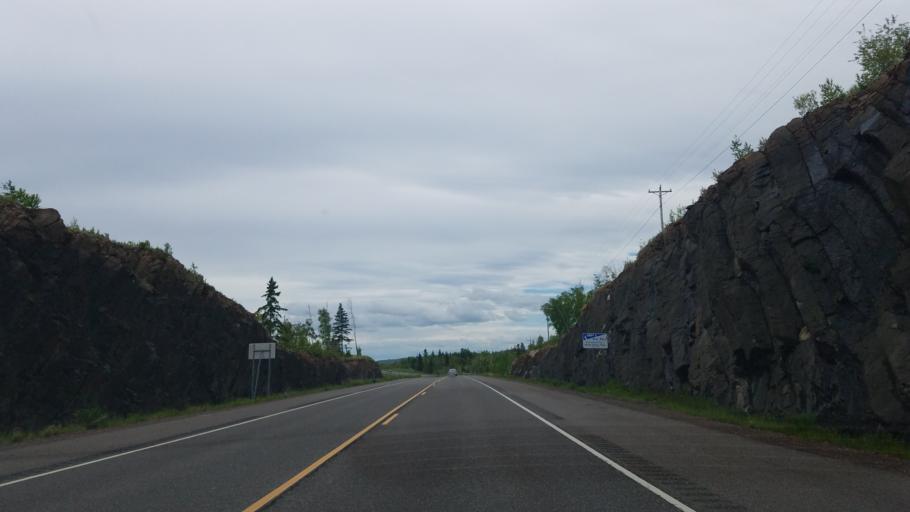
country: US
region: Minnesota
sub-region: Lake County
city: Silver Bay
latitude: 47.1996
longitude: -91.3805
